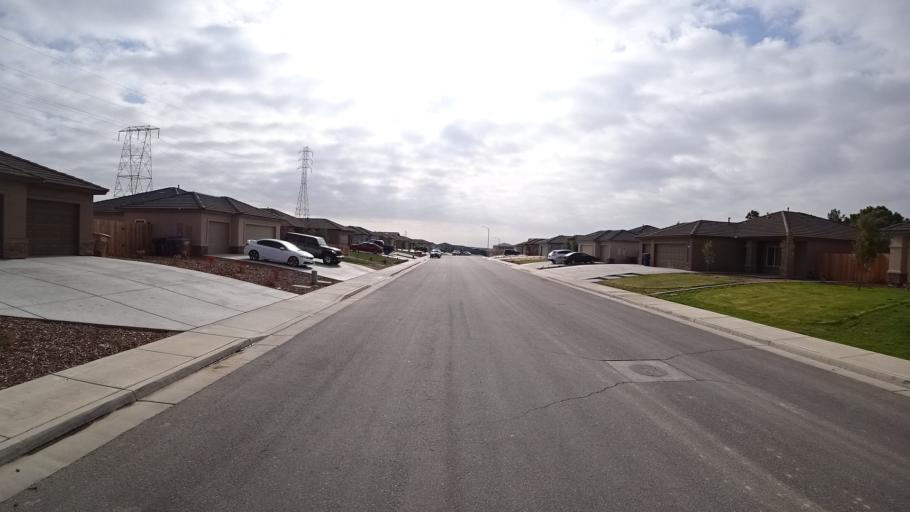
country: US
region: California
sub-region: Kern County
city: Bakersfield
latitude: 35.3893
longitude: -118.9253
